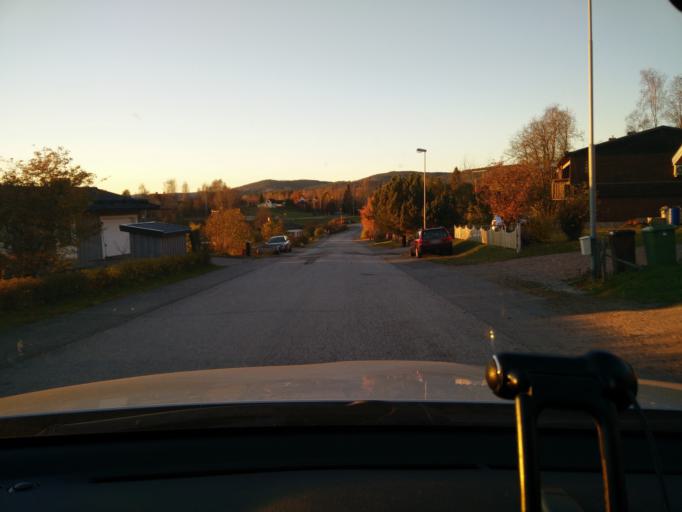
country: SE
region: Vaesternorrland
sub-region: Sundsvalls Kommun
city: Matfors
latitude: 62.3509
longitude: 17.0441
